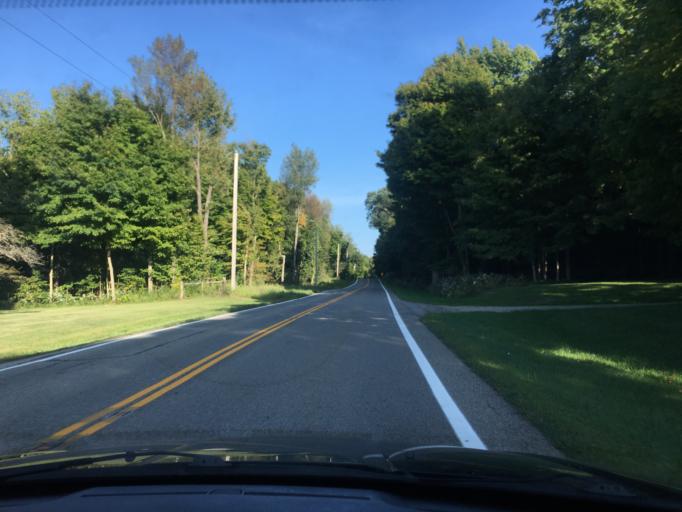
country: US
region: Ohio
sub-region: Logan County
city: West Liberty
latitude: 40.2657
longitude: -83.6724
